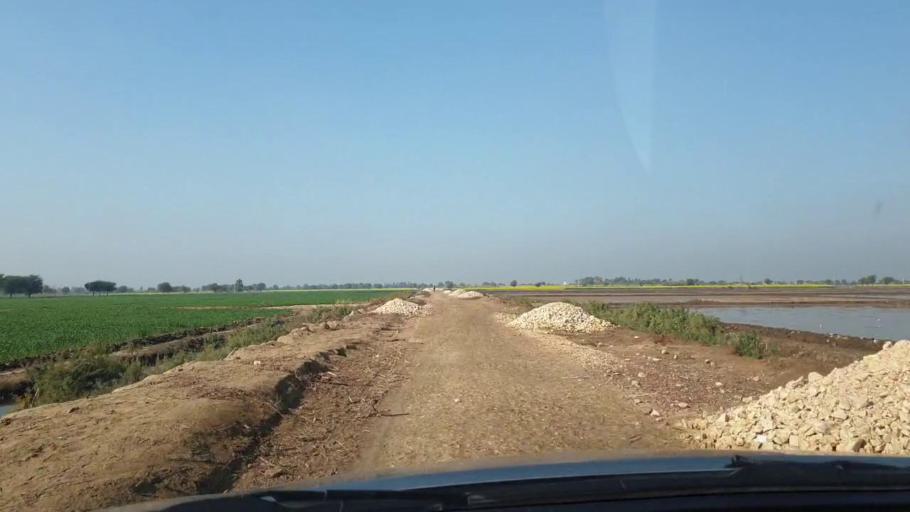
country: PK
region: Sindh
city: Berani
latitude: 25.8291
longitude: 68.9255
